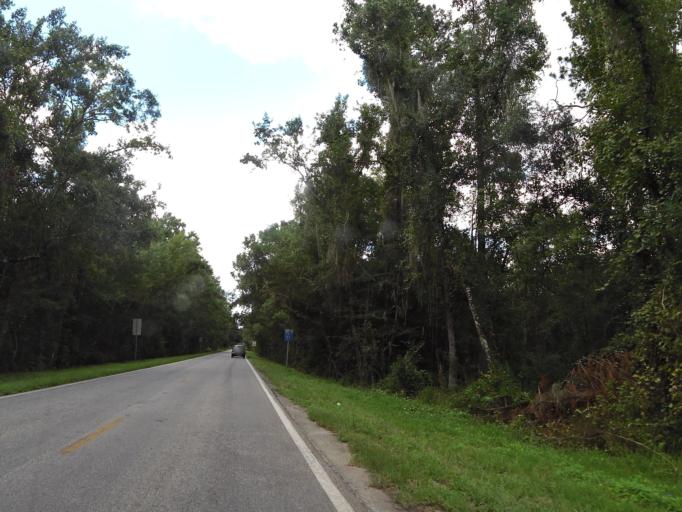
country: US
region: Florida
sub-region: Putnam County
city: East Palatka
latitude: 29.7779
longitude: -81.4868
